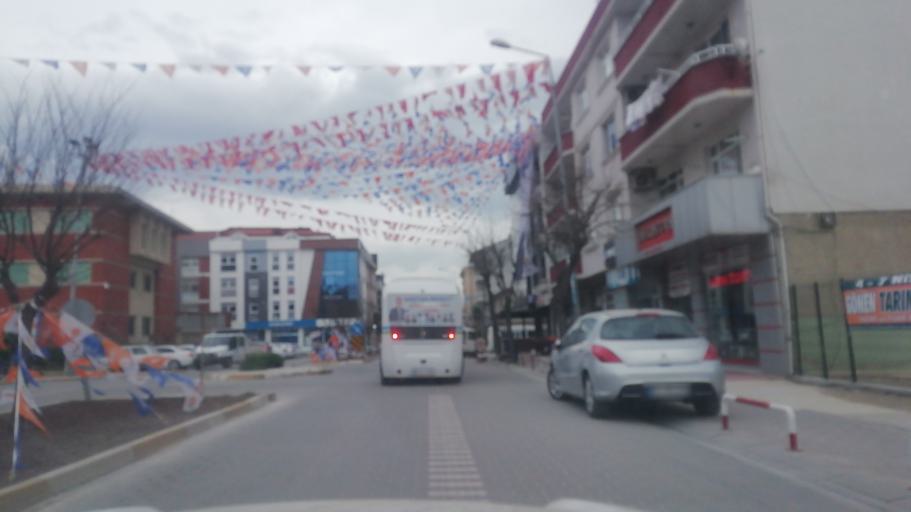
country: TR
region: Balikesir
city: Gonen
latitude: 40.1046
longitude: 27.6536
